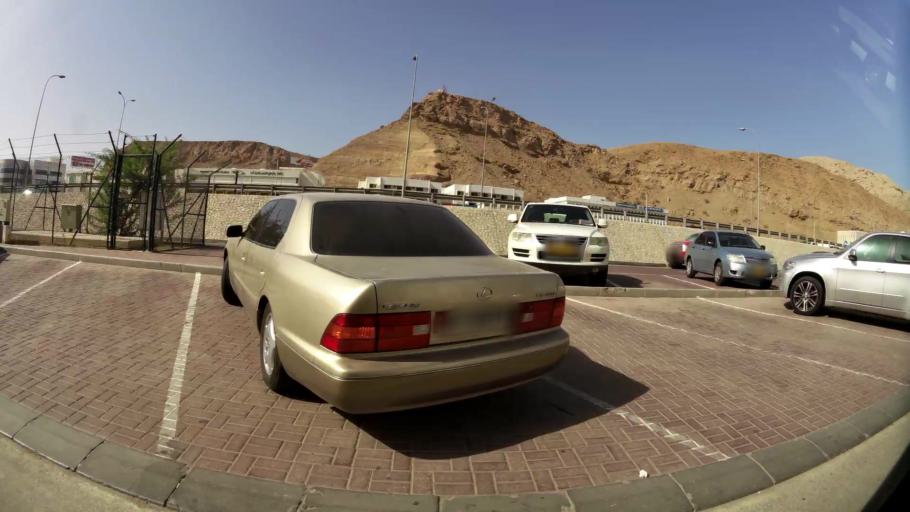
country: OM
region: Muhafazat Masqat
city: Muscat
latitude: 23.6006
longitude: 58.5159
